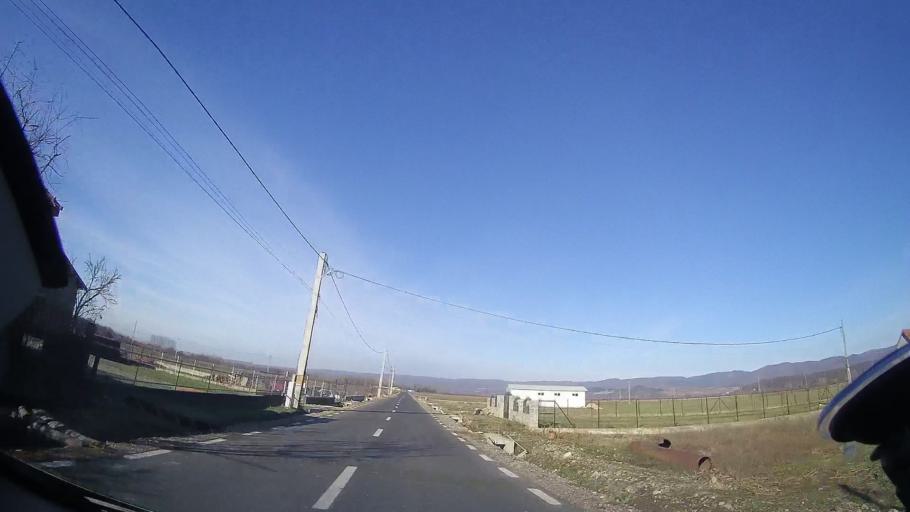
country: RO
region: Bihor
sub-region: Comuna Vadu Crisului
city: Vadu Crisului
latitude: 46.9933
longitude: 22.5081
